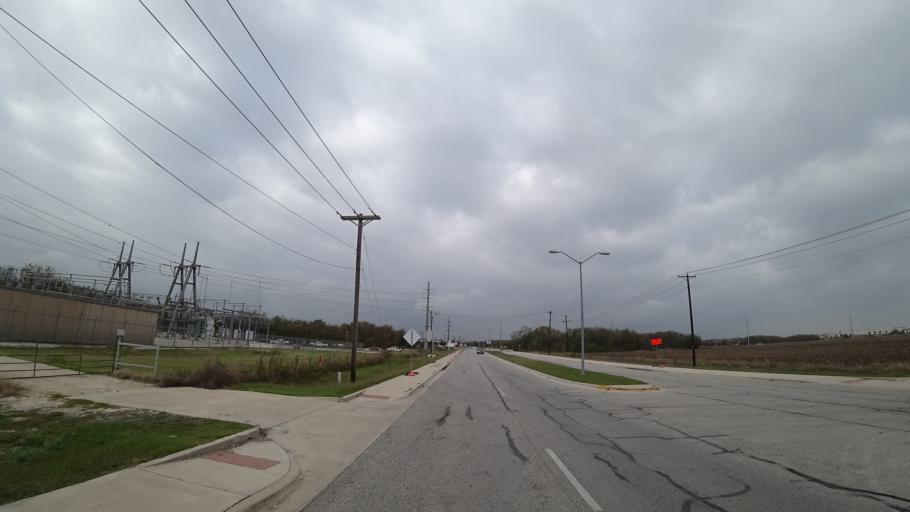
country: US
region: Texas
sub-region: Travis County
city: Pflugerville
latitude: 30.4543
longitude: -97.5992
